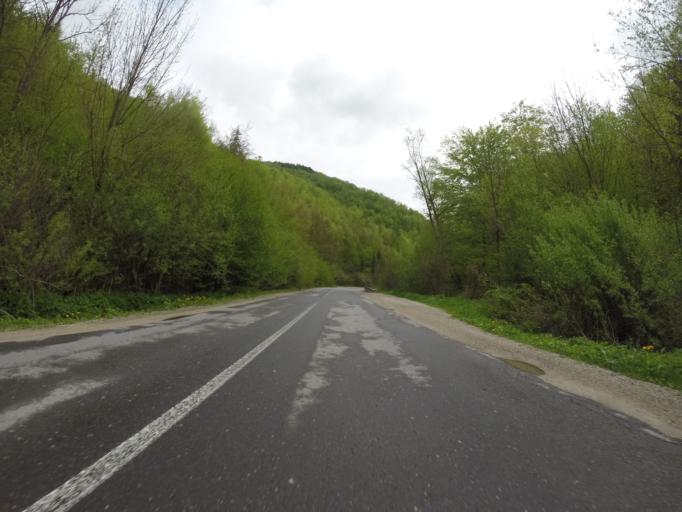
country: SK
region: Banskobystricky
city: Tisovec
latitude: 48.6894
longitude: 19.9174
